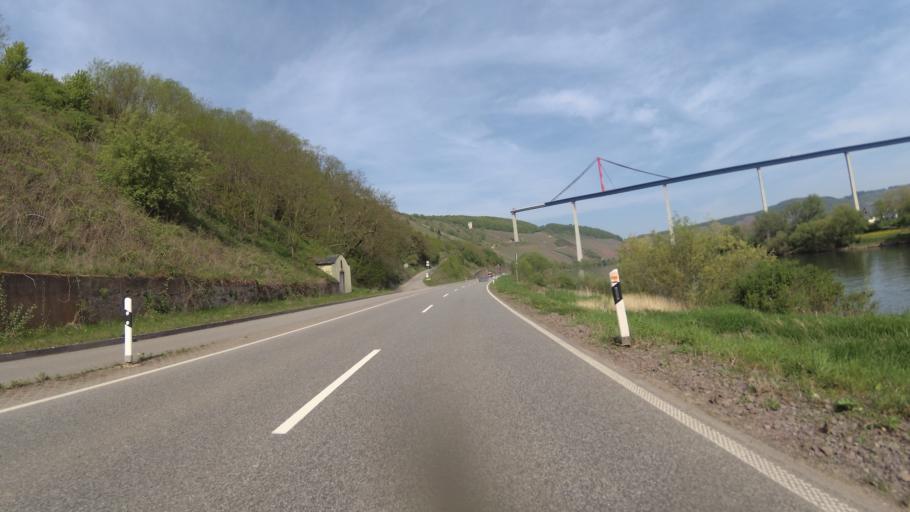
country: DE
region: Rheinland-Pfalz
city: Urzig
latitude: 49.9605
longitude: 6.9980
